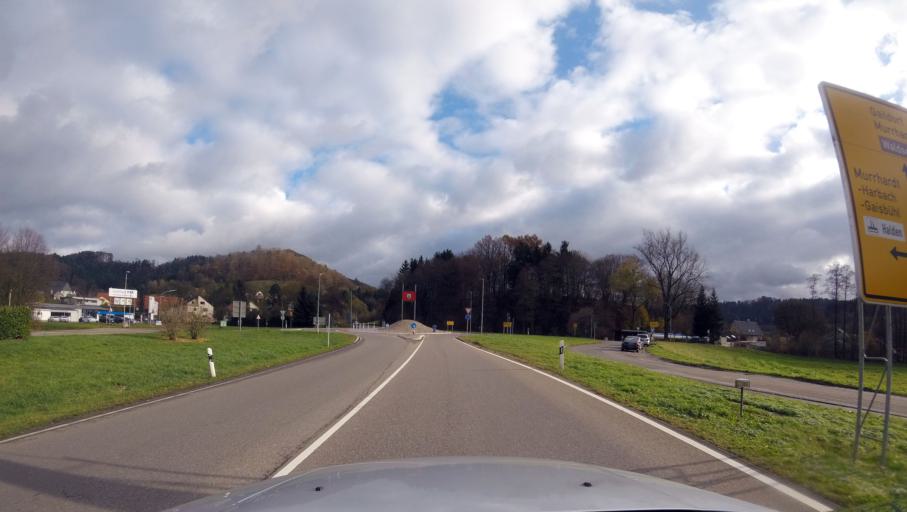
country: DE
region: Baden-Wuerttemberg
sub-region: Regierungsbezirk Stuttgart
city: Murrhardt
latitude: 48.9889
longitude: 9.5514
